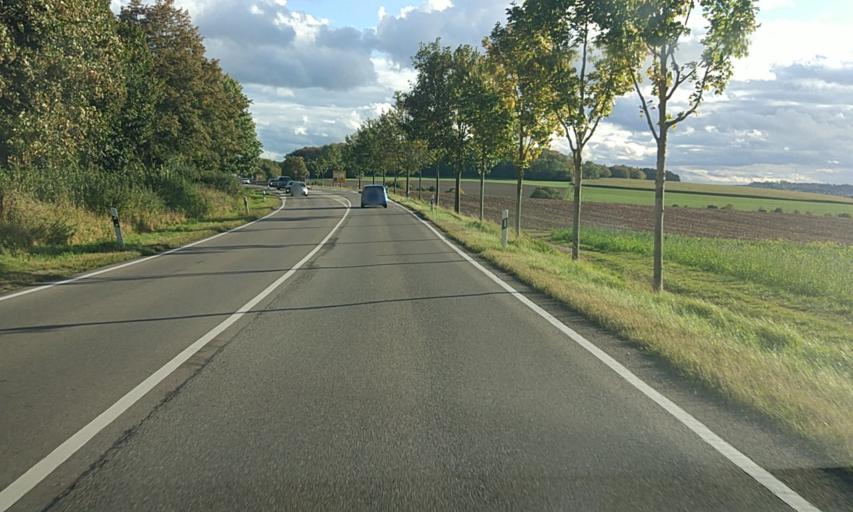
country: DE
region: Baden-Wuerttemberg
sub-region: Tuebingen Region
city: Ulm
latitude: 48.4293
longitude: 9.9820
